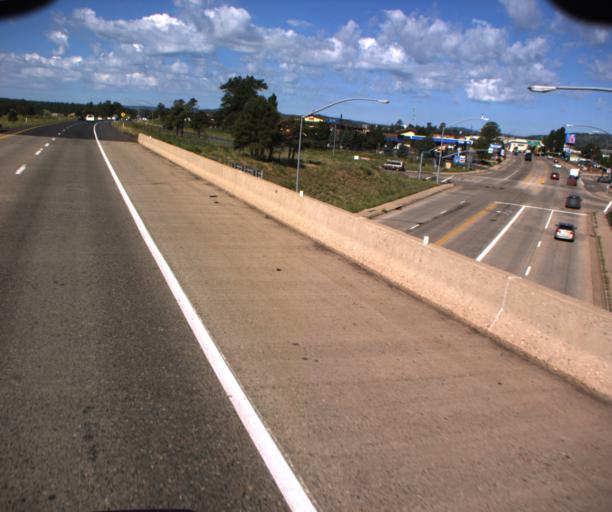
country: US
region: Arizona
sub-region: Coconino County
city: Flagstaff
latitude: 35.1920
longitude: -111.6218
